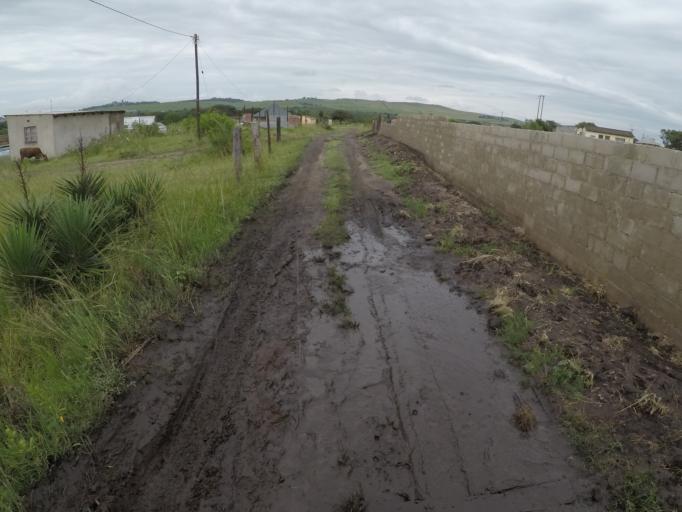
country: ZA
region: KwaZulu-Natal
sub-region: uThungulu District Municipality
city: Empangeni
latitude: -28.7122
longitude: 31.8644
